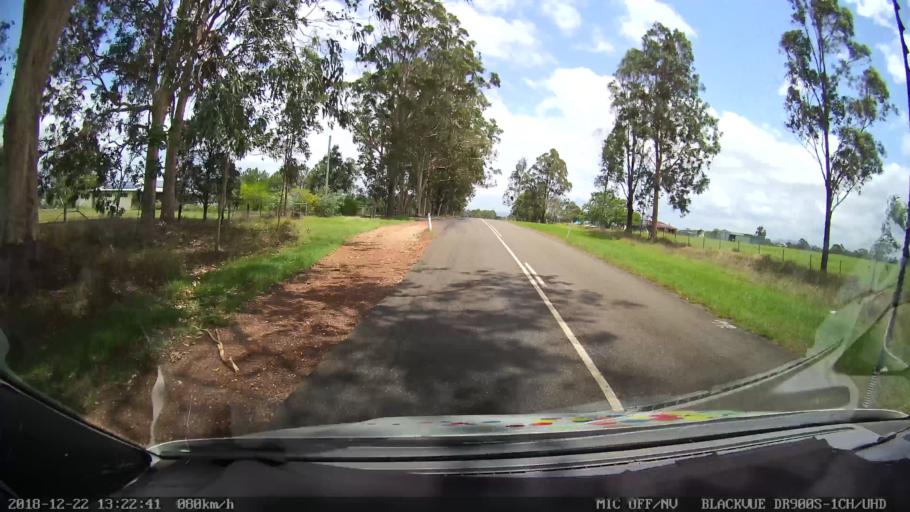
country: AU
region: New South Wales
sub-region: Clarence Valley
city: Coutts Crossing
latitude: -29.7897
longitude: 152.9105
